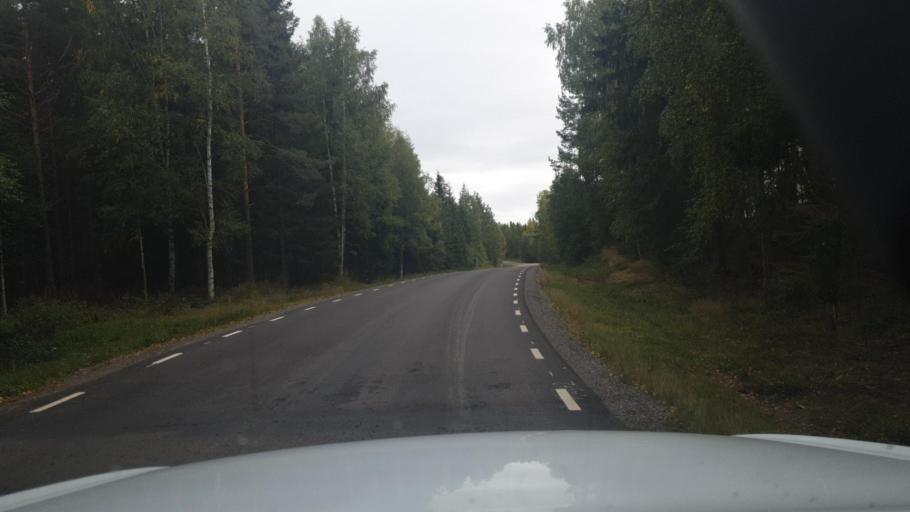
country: SE
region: Vaermland
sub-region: Torsby Kommun
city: Torsby
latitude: 60.0047
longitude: 12.7187
